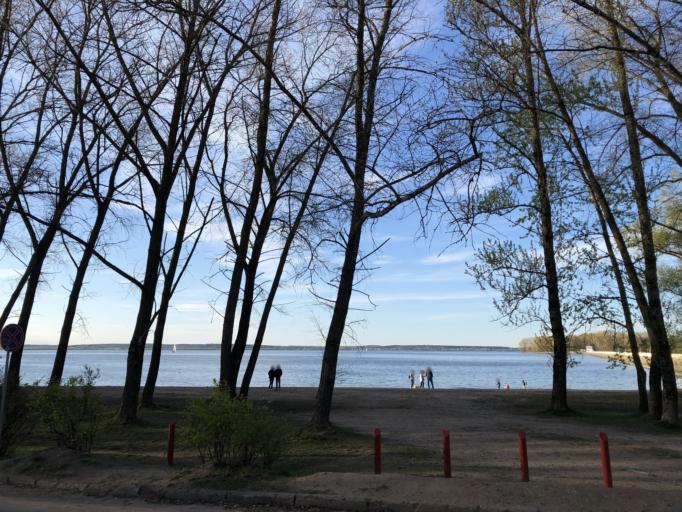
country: BY
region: Minsk
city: Zhdanovichy
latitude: 53.9501
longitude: 27.3768
